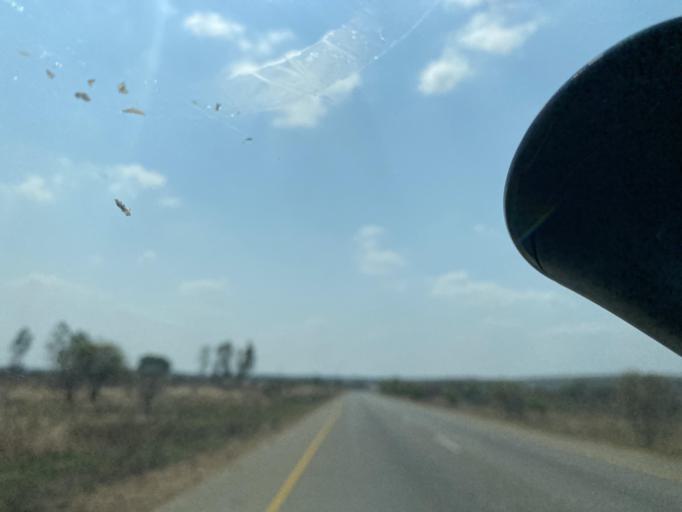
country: ZM
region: Lusaka
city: Chongwe
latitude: -15.5468
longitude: 28.6693
